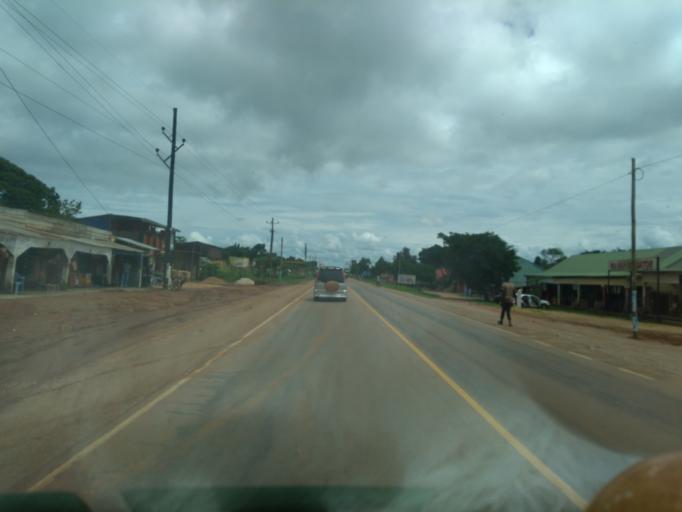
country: UG
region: Central Region
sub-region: Butambala District
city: Gombe
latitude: 0.0000
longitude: 32.0400
